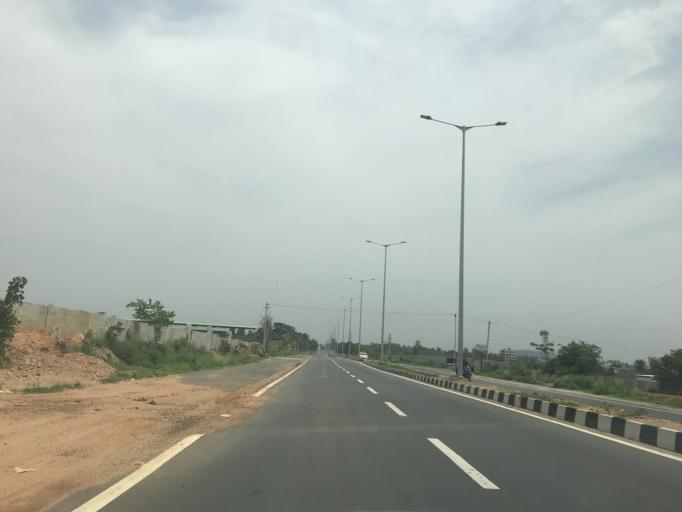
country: IN
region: Karnataka
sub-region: Bangalore Urban
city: Yelahanka
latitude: 13.1150
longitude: 77.6681
